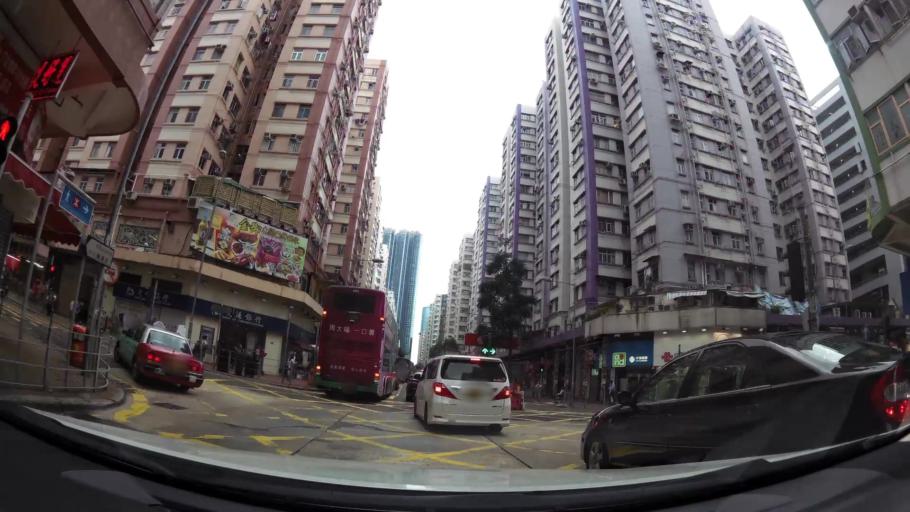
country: HK
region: Kowloon City
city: Kowloon
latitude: 22.3066
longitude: 114.1871
